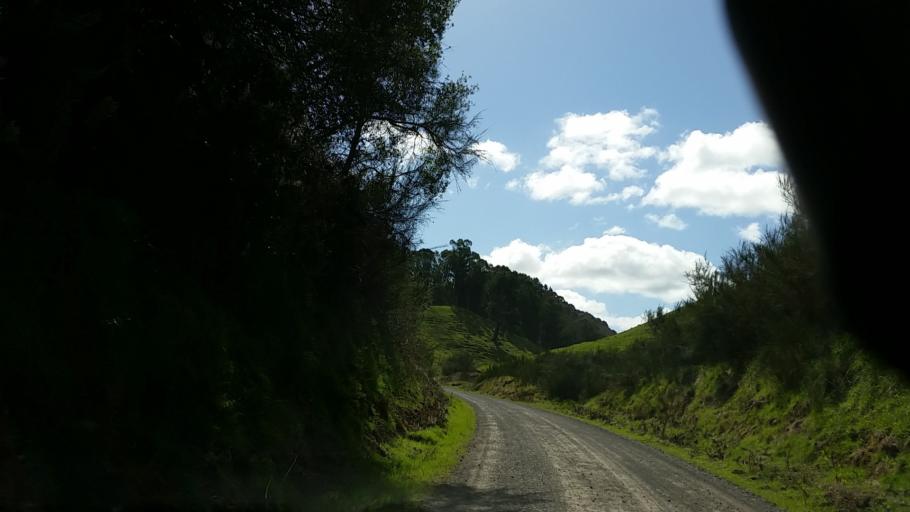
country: NZ
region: Waikato
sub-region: Taupo District
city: Taupo
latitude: -38.4943
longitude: 176.2069
